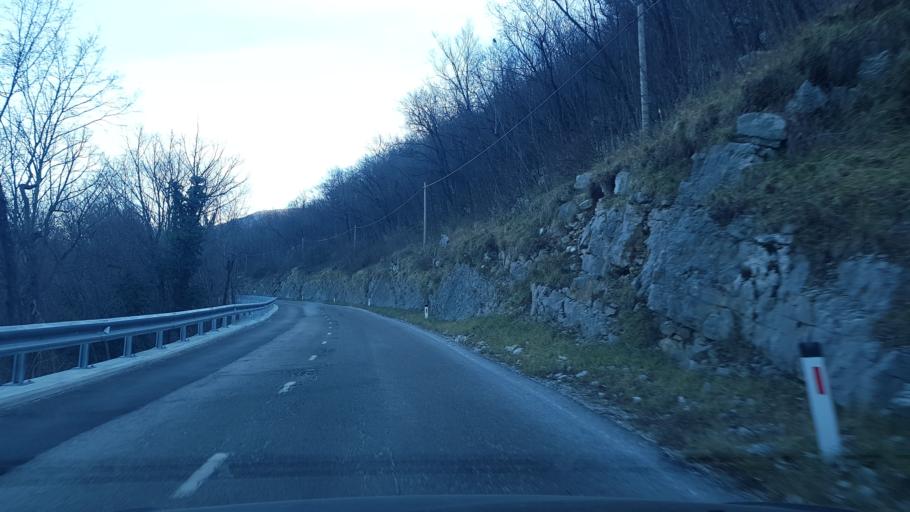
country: SI
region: Nova Gorica
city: Kromberk
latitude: 46.0078
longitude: 13.6962
